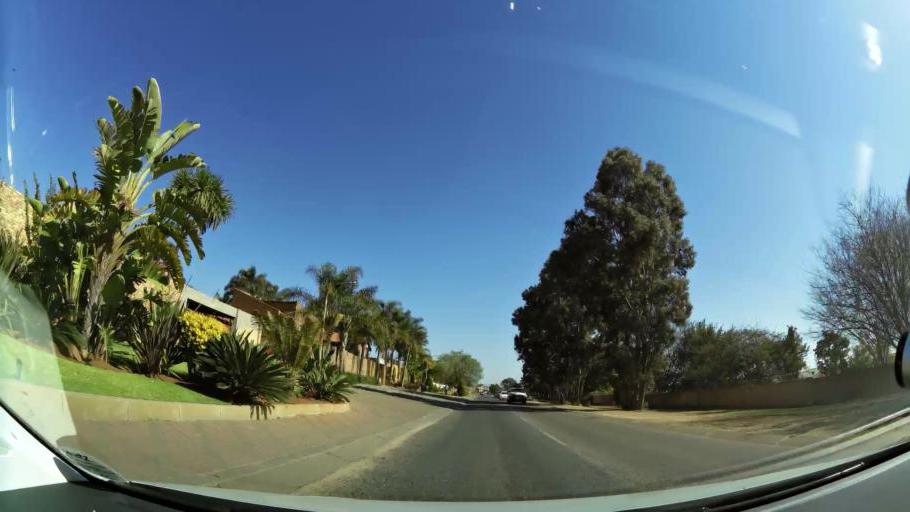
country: ZA
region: Gauteng
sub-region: City of Johannesburg Metropolitan Municipality
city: Modderfontein
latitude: -26.0716
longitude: 28.1982
